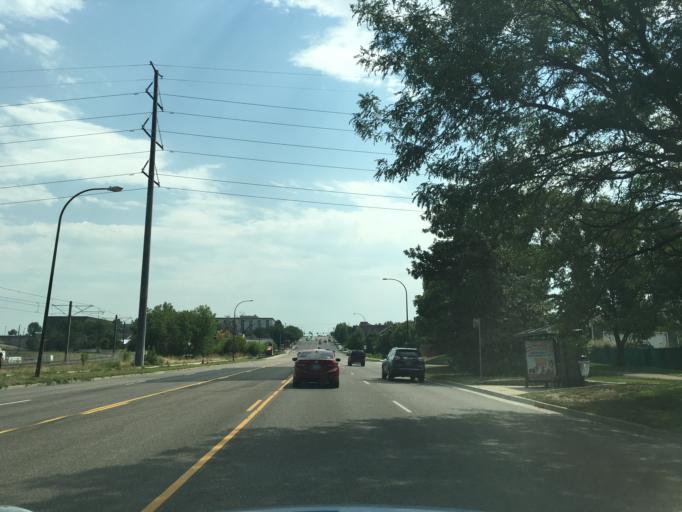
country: US
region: Colorado
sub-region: Jefferson County
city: Applewood
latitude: 39.7337
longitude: -105.1285
